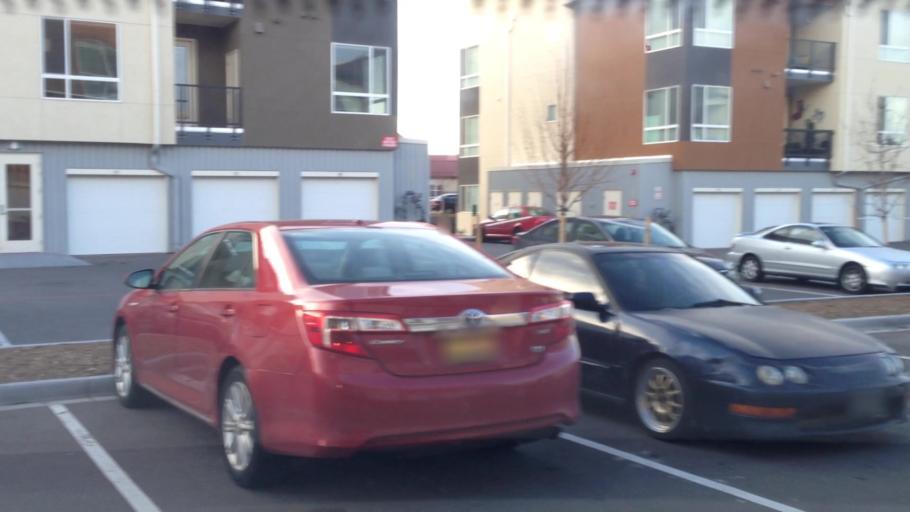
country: US
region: Colorado
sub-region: Adams County
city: Aurora
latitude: 39.6684
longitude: -104.8255
